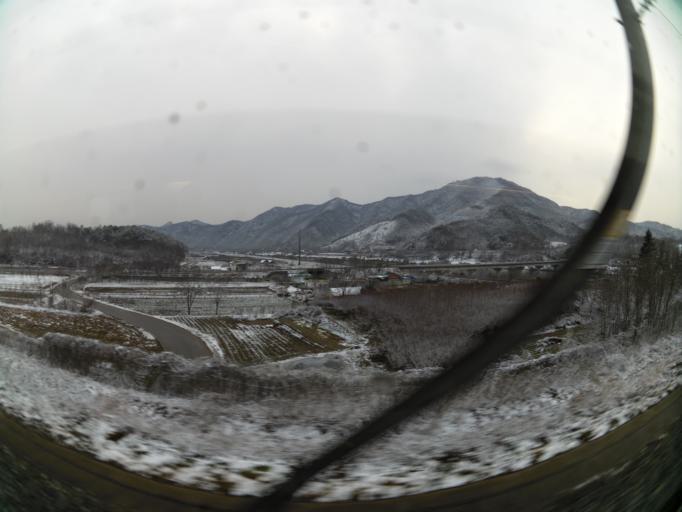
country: KR
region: Chungcheongbuk-do
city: Okcheon
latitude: 36.2418
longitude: 127.6728
